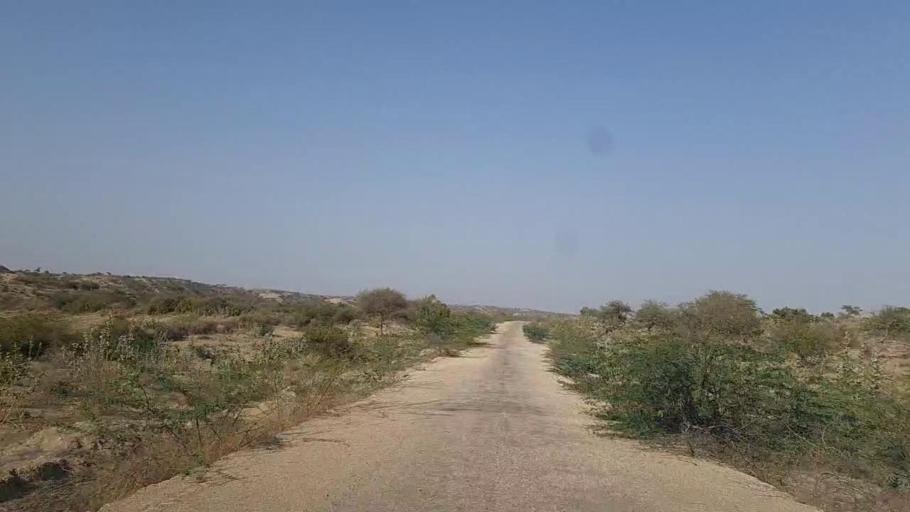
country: PK
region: Sindh
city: Naukot
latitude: 24.6205
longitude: 69.3489
